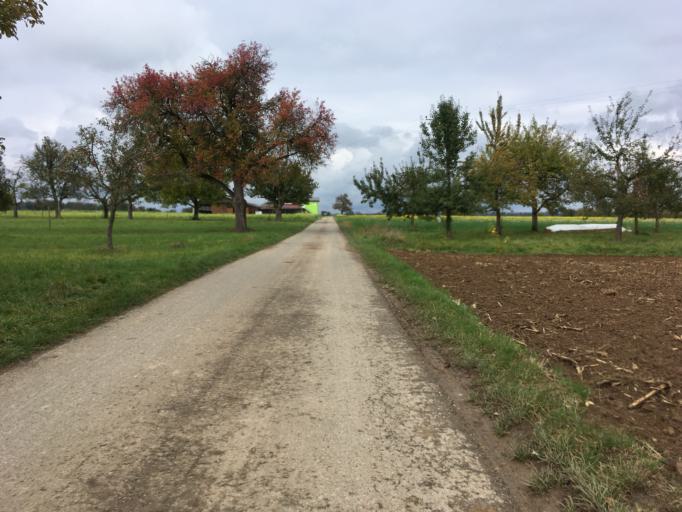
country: DE
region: Baden-Wuerttemberg
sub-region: Tuebingen Region
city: Gomaringen
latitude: 48.4919
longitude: 9.0940
